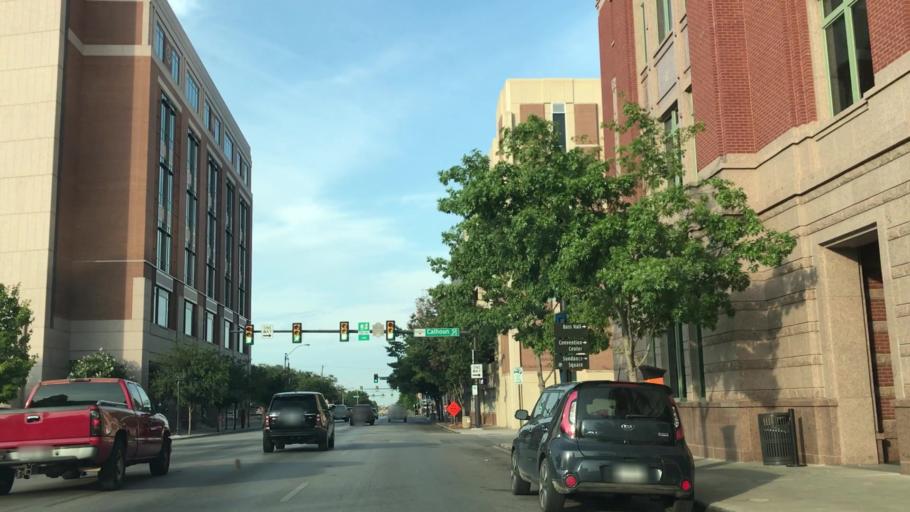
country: US
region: Texas
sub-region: Tarrant County
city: Fort Worth
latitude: 32.7576
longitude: -97.3318
